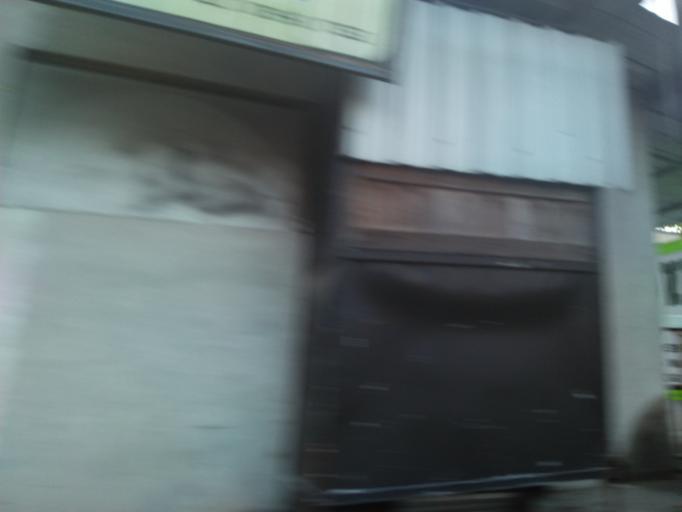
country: ID
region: Daerah Istimewa Yogyakarta
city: Sewon
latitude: -7.8557
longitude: 110.4095
